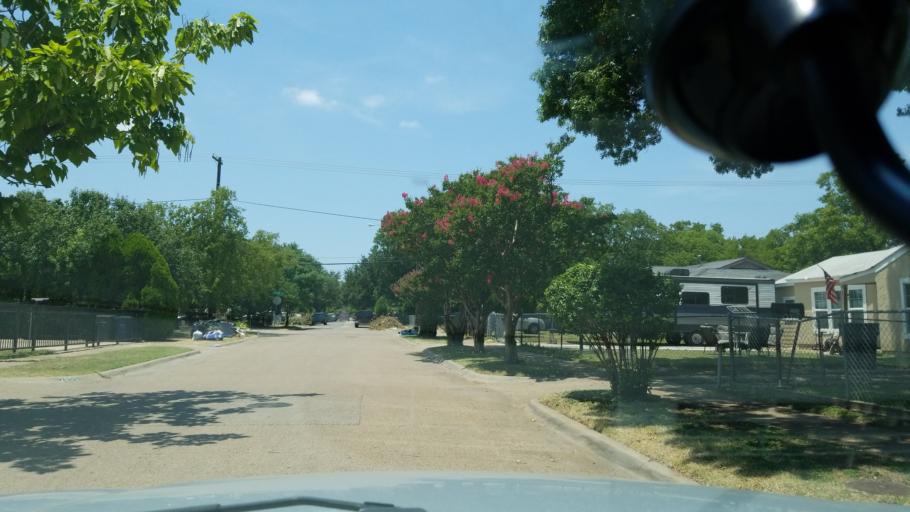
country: US
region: Texas
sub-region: Dallas County
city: Cockrell Hill
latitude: 32.7254
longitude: -96.8682
